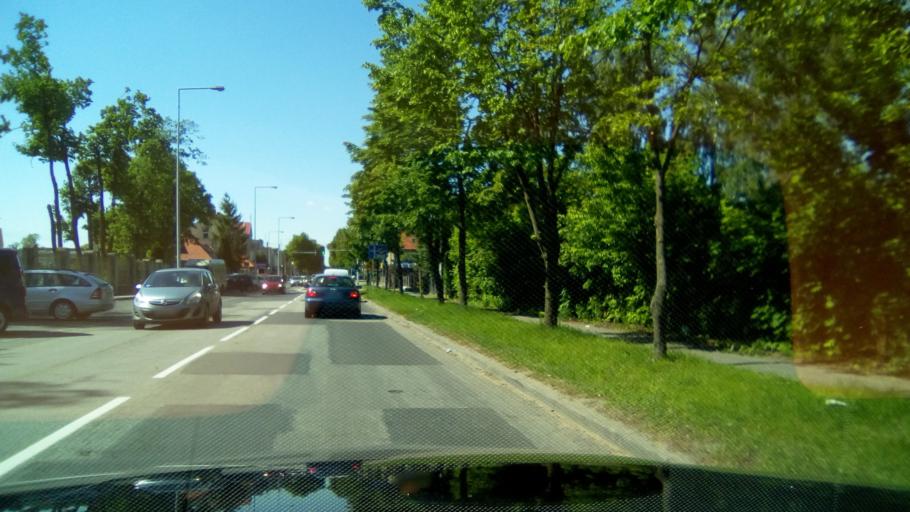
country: PL
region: Greater Poland Voivodeship
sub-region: Powiat gnieznienski
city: Gniezno
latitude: 52.5196
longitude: 17.6068
